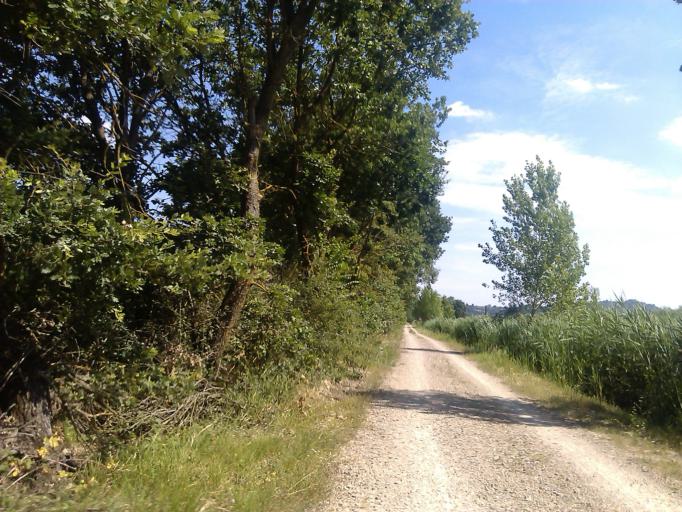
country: IT
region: Tuscany
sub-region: Provincia di Siena
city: Chiusi
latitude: 43.0625
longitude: 11.9323
